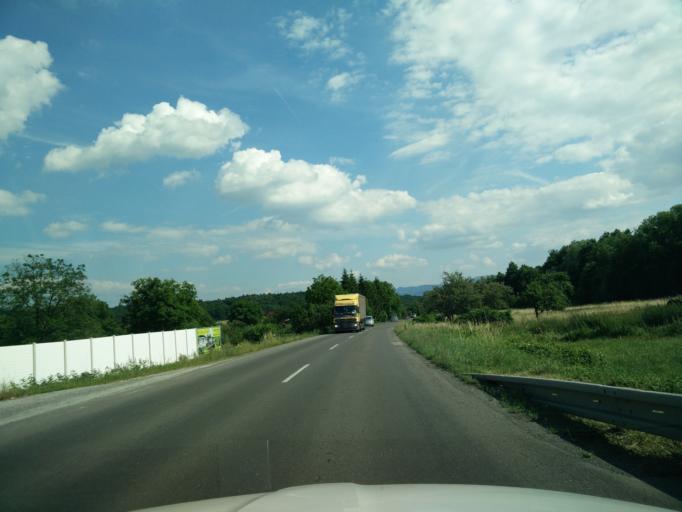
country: SK
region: Nitriansky
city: Prievidza
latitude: 48.8526
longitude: 18.6441
